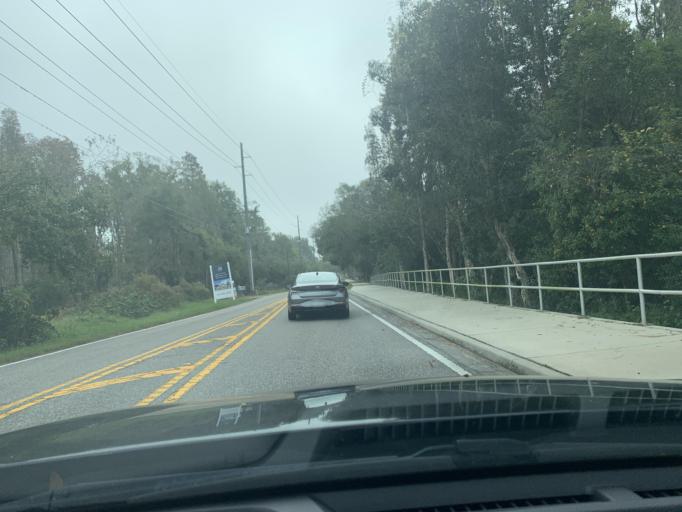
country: US
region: Florida
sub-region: Hillsborough County
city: Lutz
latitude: 28.1277
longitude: -82.4869
